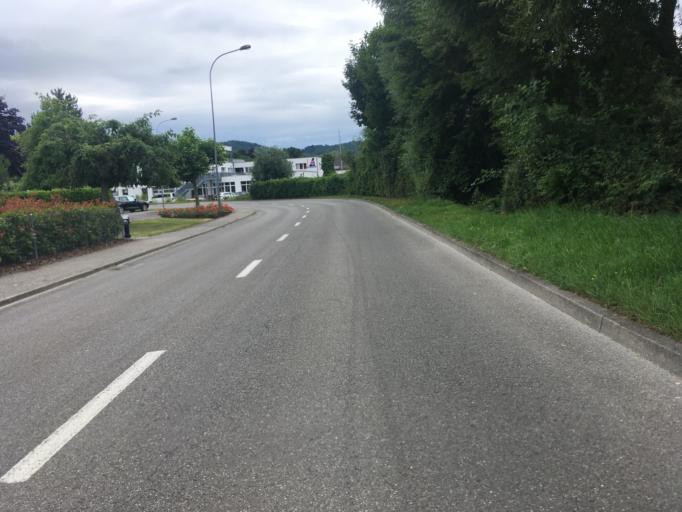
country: CH
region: Fribourg
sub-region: Broye District
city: Estavayer-le-Lac
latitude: 46.8480
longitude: 6.8383
